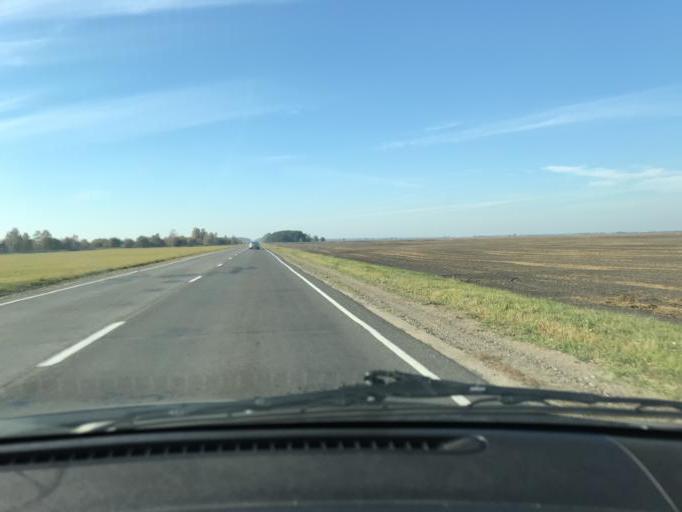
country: BY
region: Brest
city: Asnyezhytsy
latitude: 52.2710
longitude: 26.3667
